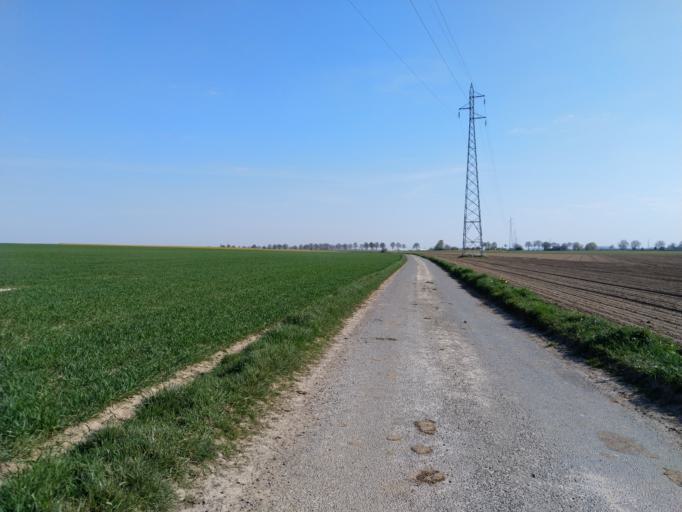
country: BE
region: Wallonia
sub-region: Province du Hainaut
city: Lens
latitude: 50.5576
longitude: 3.8798
